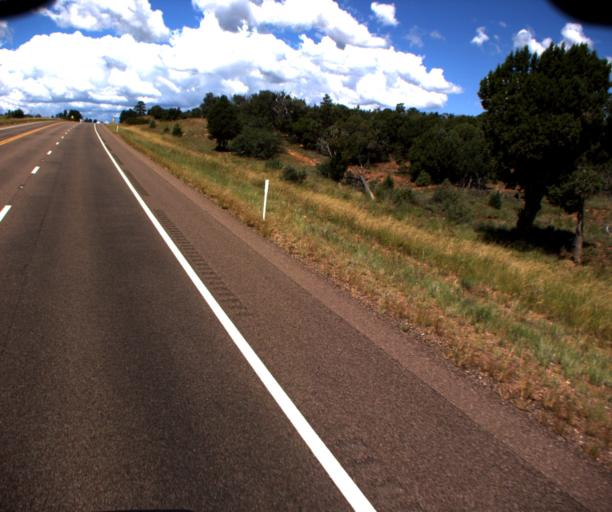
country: US
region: Arizona
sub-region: Navajo County
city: Linden
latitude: 34.3649
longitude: -110.3527
